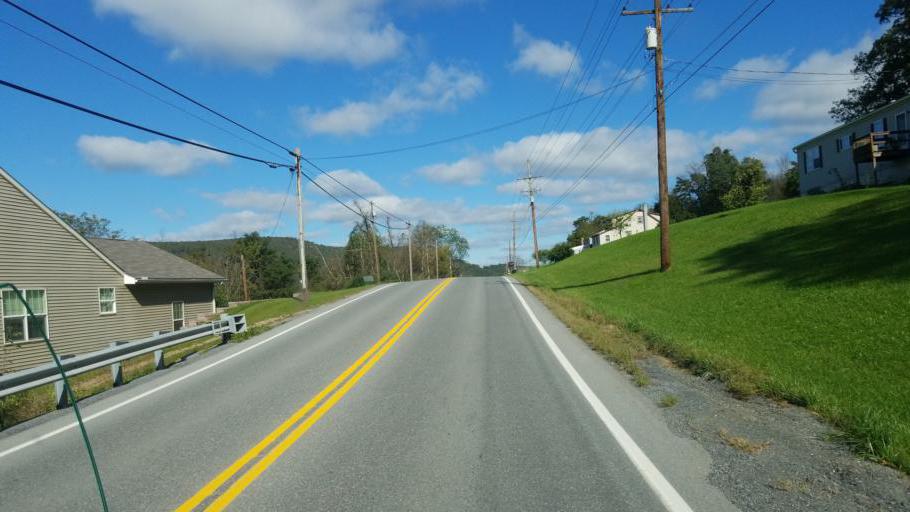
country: US
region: Pennsylvania
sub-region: Fulton County
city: McConnellsburg
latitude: 39.9427
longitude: -78.0202
